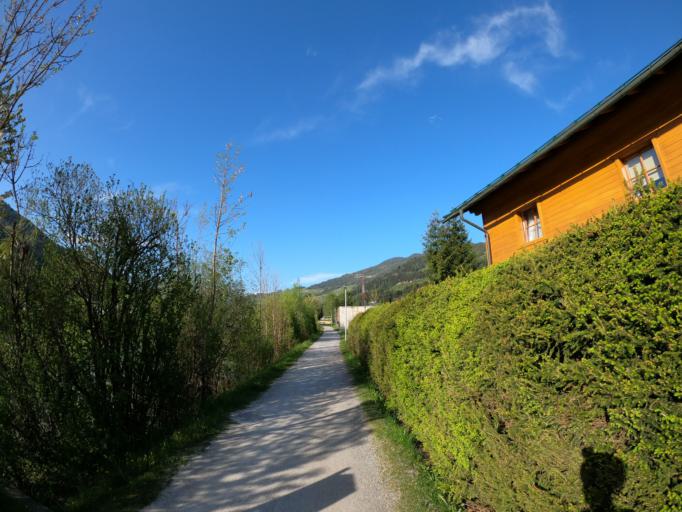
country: AT
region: Salzburg
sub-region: Politischer Bezirk Sankt Johann im Pongau
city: Sankt Johann im Pongau
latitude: 47.3518
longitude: 13.1995
